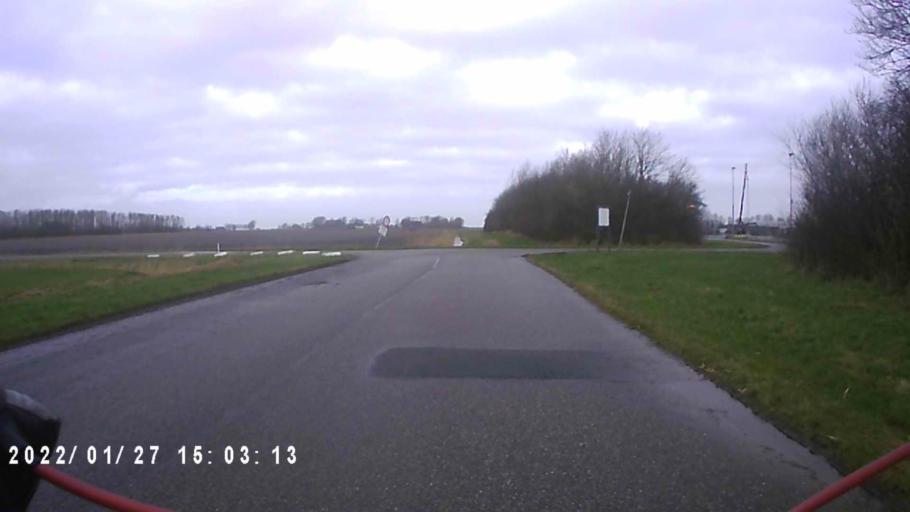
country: NL
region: Friesland
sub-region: Gemeente Dongeradeel
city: Anjum
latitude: 53.3703
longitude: 6.1483
